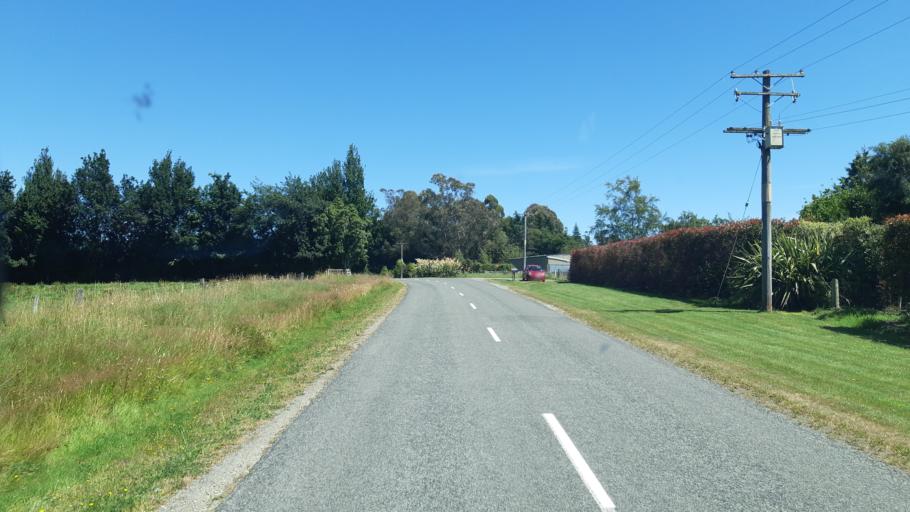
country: NZ
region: Canterbury
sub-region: Timaru District
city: Timaru
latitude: -44.4067
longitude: 171.1399
